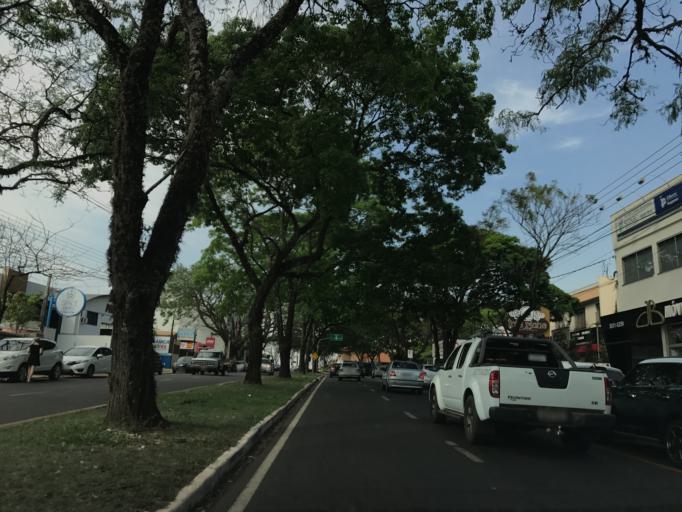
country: BR
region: Parana
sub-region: Maringa
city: Maringa
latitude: -23.4370
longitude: -51.9351
